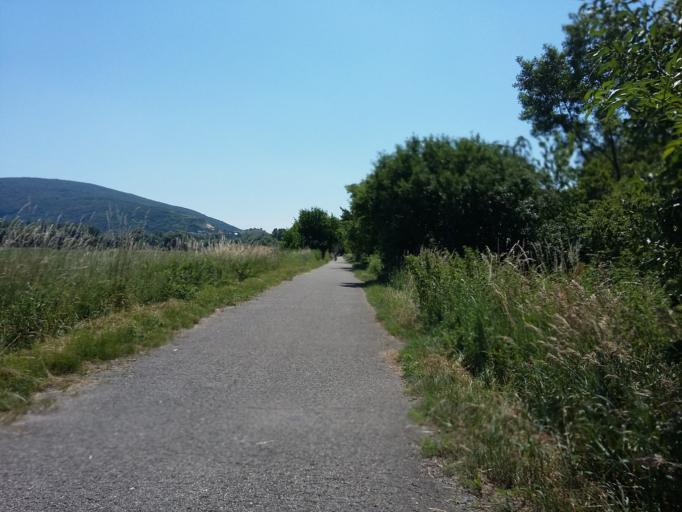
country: AT
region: Lower Austria
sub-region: Politischer Bezirk Bruck an der Leitha
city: Hainburg an der Donau
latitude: 48.2183
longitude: 16.9632
